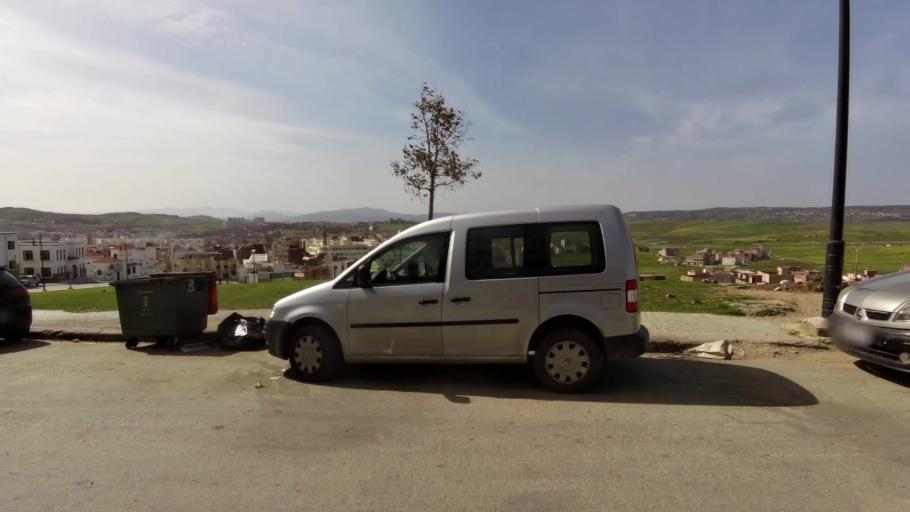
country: MA
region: Tanger-Tetouan
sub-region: Tanger-Assilah
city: Tangier
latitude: 35.7301
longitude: -5.8146
